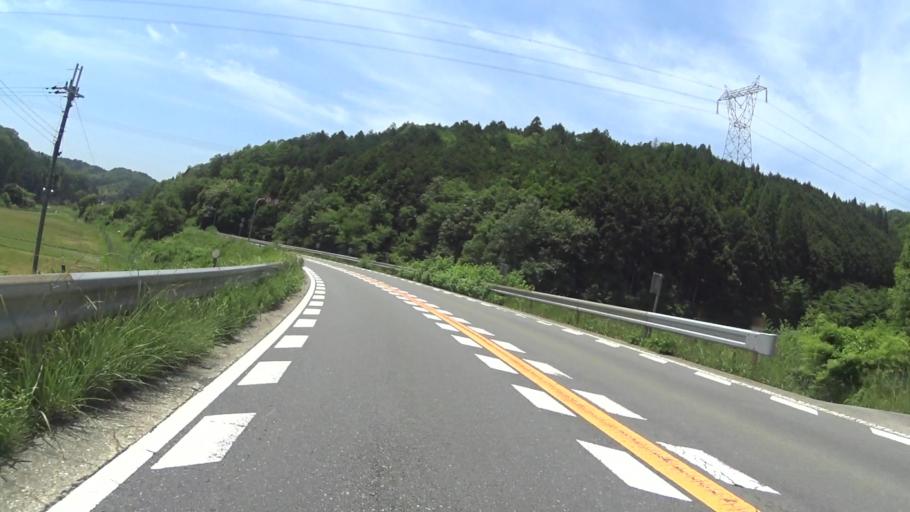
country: JP
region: Kyoto
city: Ayabe
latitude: 35.1901
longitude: 135.3337
